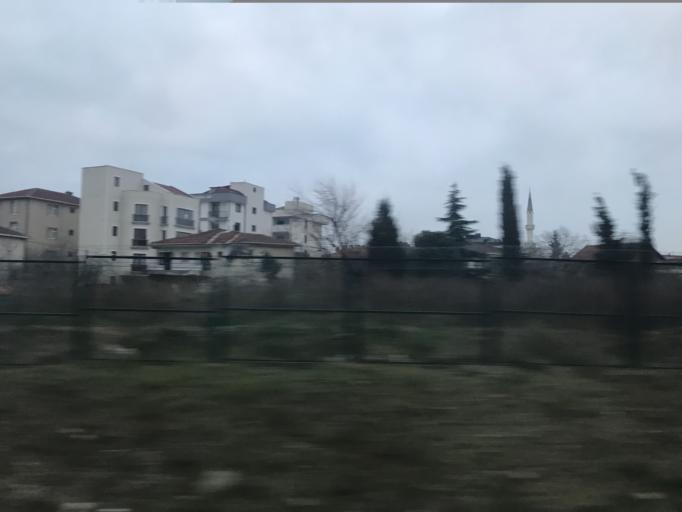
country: TR
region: Istanbul
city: Icmeler
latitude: 40.8267
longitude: 29.3264
